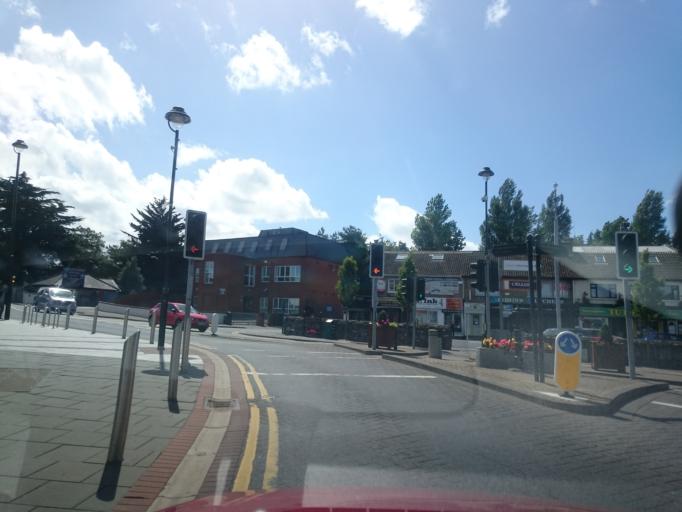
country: IE
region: Leinster
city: Clondalkin
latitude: 53.3205
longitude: -6.3944
